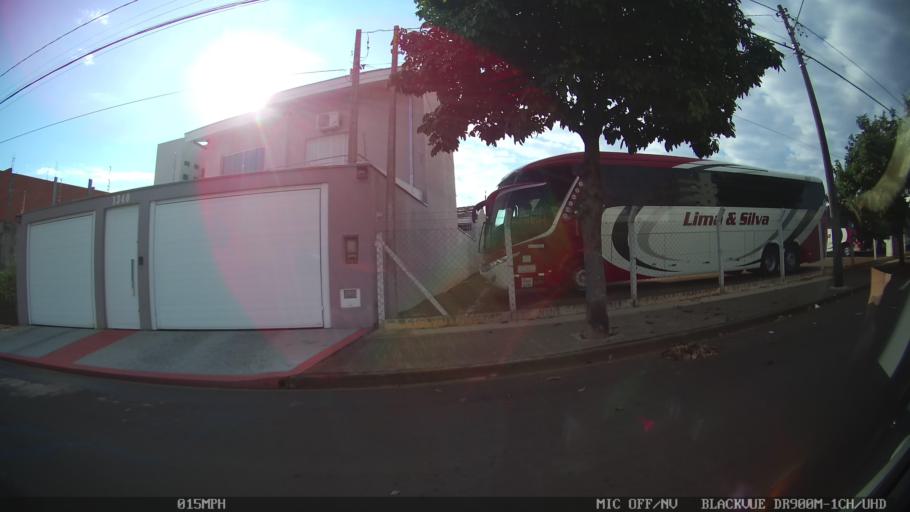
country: BR
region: Sao Paulo
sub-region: Americana
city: Americana
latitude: -22.7322
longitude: -47.3605
